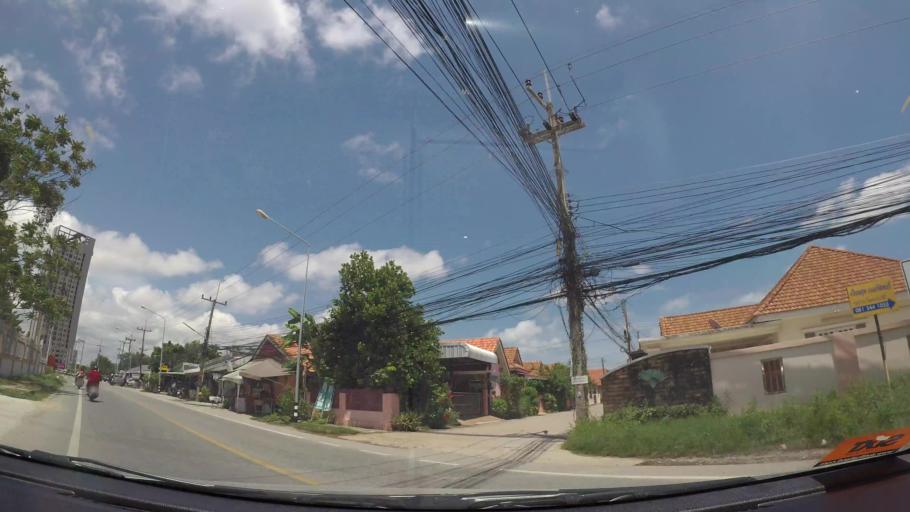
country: TH
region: Rayong
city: Rayong
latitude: 12.6946
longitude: 101.2659
